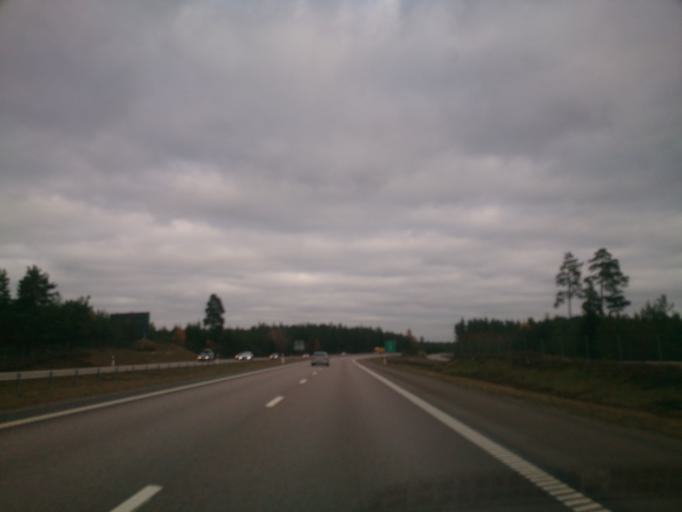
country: SE
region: OEstergoetland
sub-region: Norrkopings Kommun
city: Krokek
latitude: 58.7164
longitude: 16.3720
